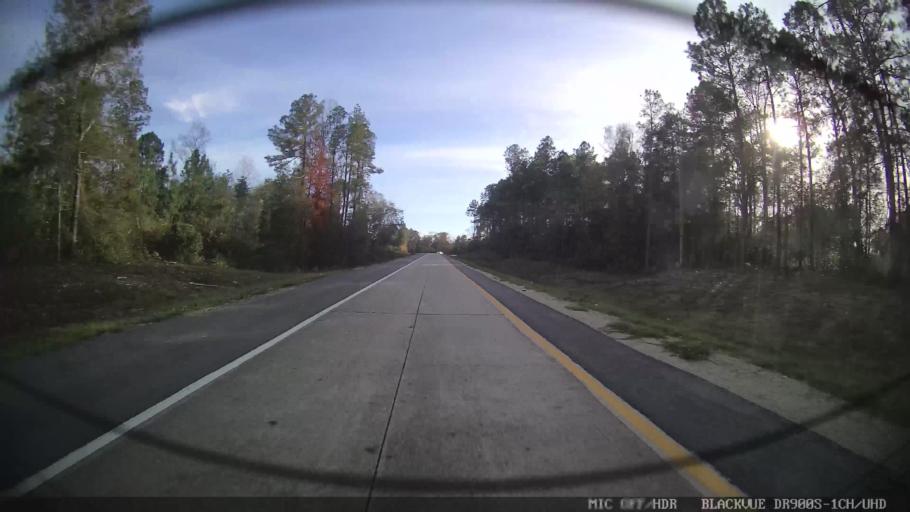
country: US
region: Mississippi
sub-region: Lamar County
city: Purvis
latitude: 31.1419
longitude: -89.3669
